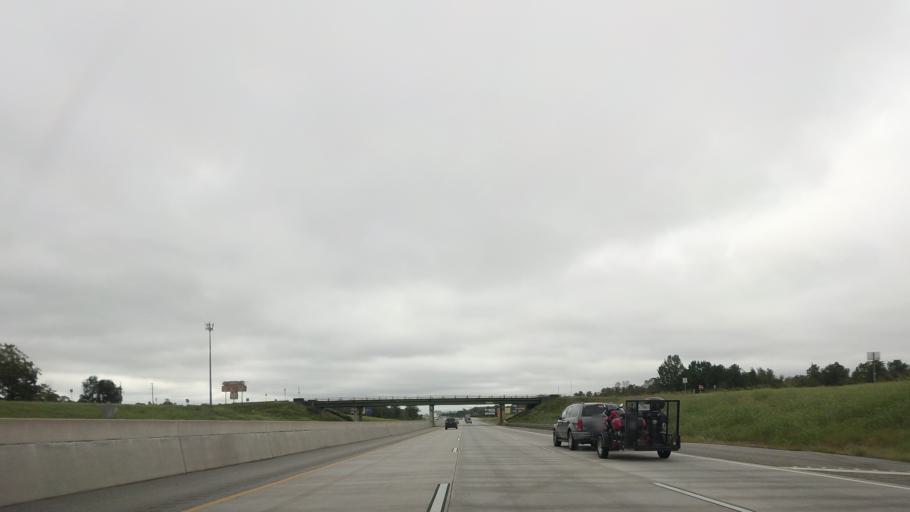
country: US
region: Georgia
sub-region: Cook County
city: Sparks
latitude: 31.1669
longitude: -83.4497
